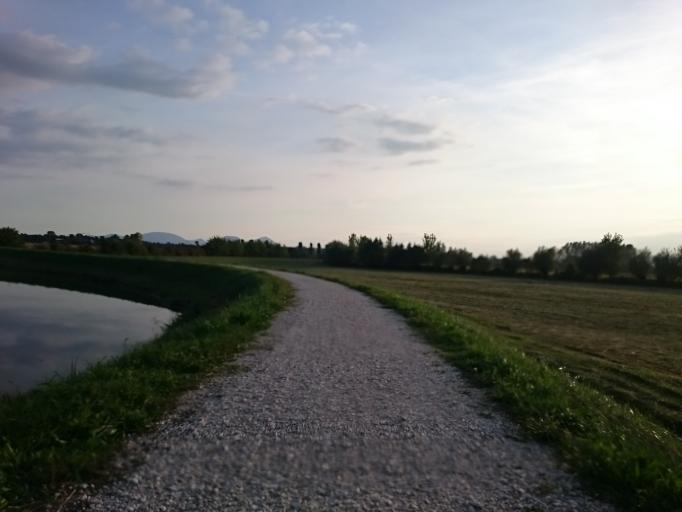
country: IT
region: Veneto
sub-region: Provincia di Vicenza
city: Camisano Vicentino
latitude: 45.5073
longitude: 11.7300
